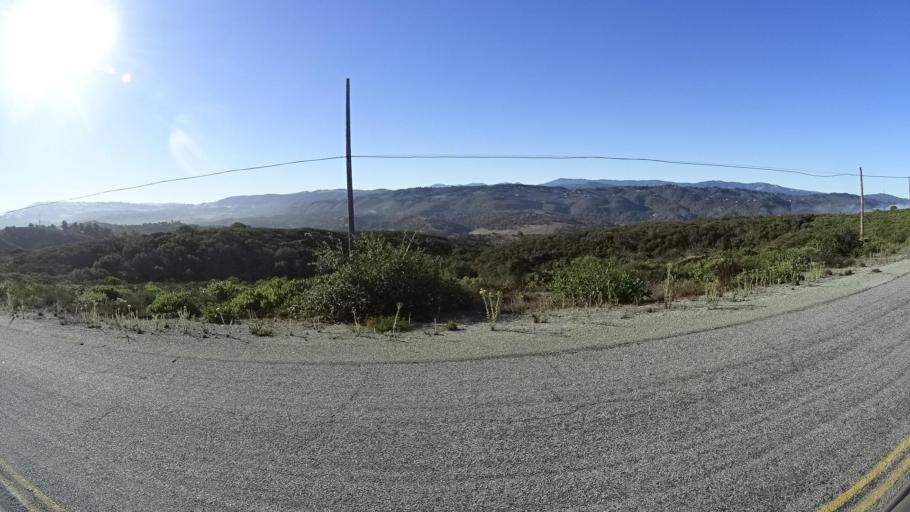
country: US
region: California
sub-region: Monterey County
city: Del Rey Oaks
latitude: 36.5870
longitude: -121.7696
